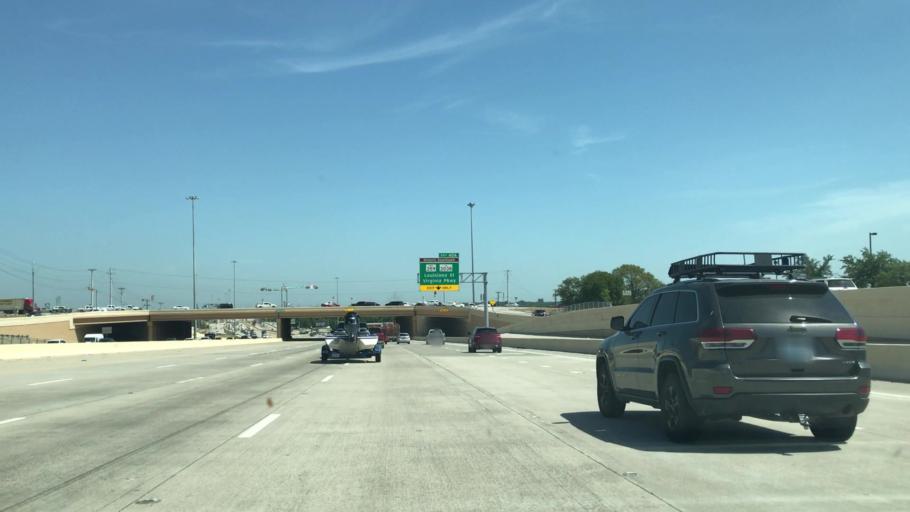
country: US
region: Texas
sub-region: Collin County
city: Fairview
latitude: 33.1697
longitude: -96.6409
